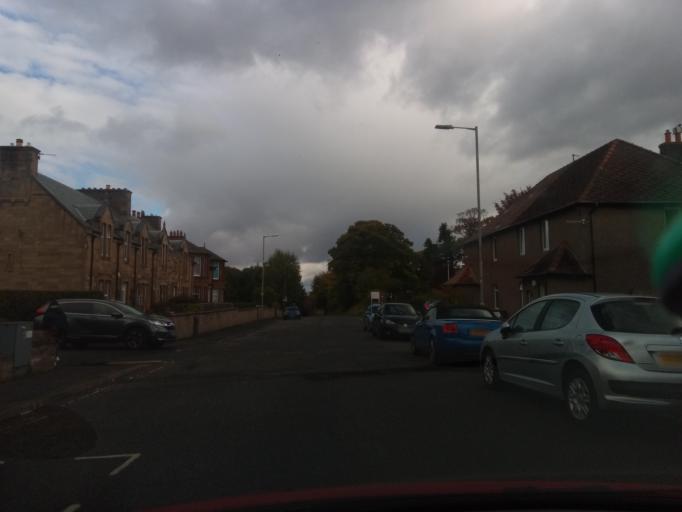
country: GB
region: Scotland
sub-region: The Scottish Borders
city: Galashiels
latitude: 55.6075
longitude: -2.7883
